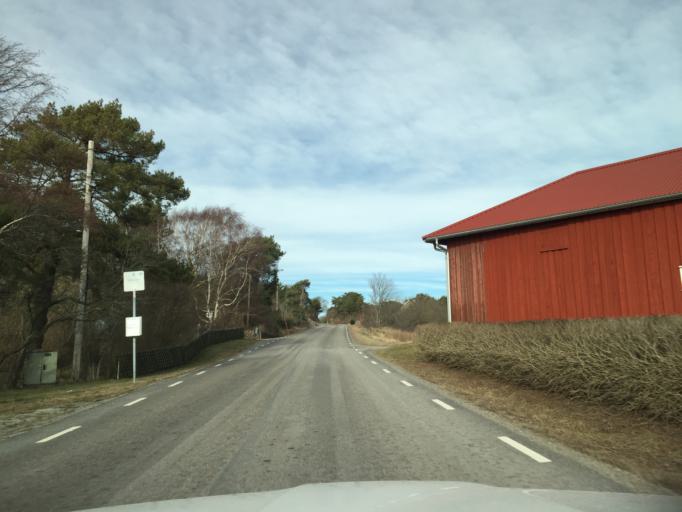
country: SE
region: Vaestra Goetaland
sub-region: Tjorns Kommun
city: Skaerhamn
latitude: 58.0215
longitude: 11.5346
